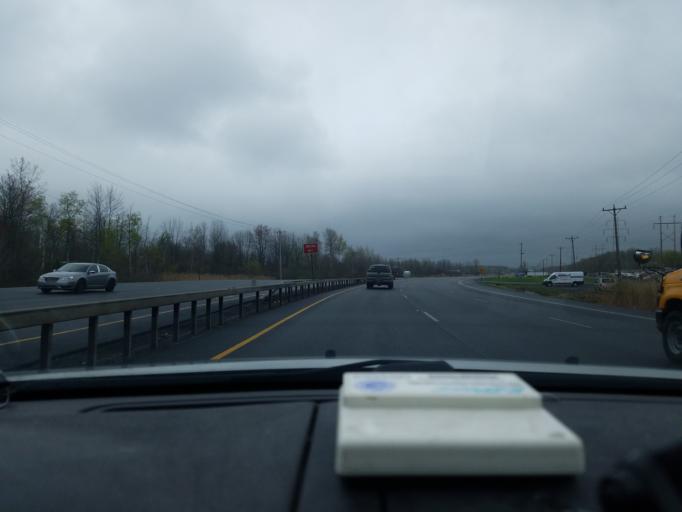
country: US
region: New York
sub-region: Onondaga County
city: North Syracuse
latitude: 43.1273
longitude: -76.0792
